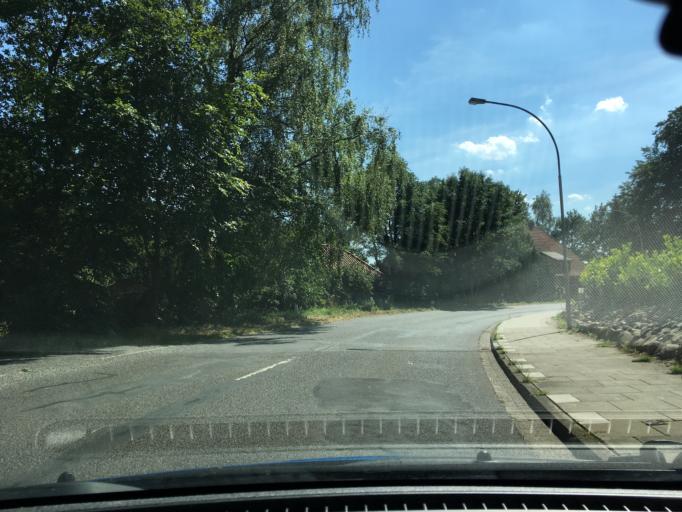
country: DE
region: Lower Saxony
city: Seevetal
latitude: 53.3919
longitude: 10.0066
